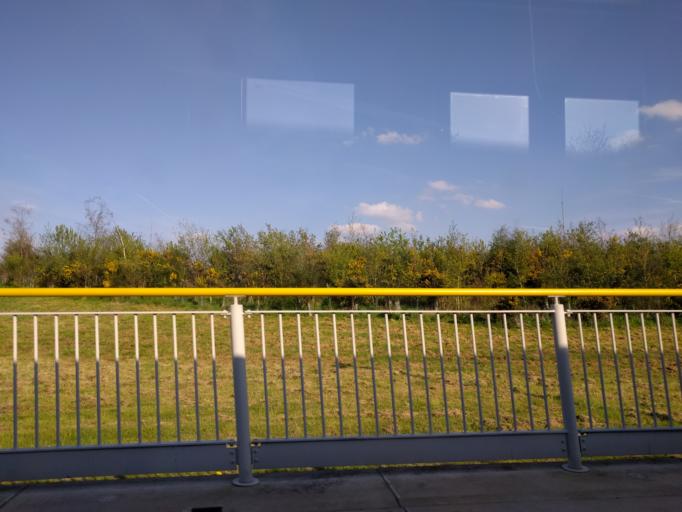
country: GB
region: England
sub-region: Manchester
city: Ringway
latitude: 53.3681
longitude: -2.2524
